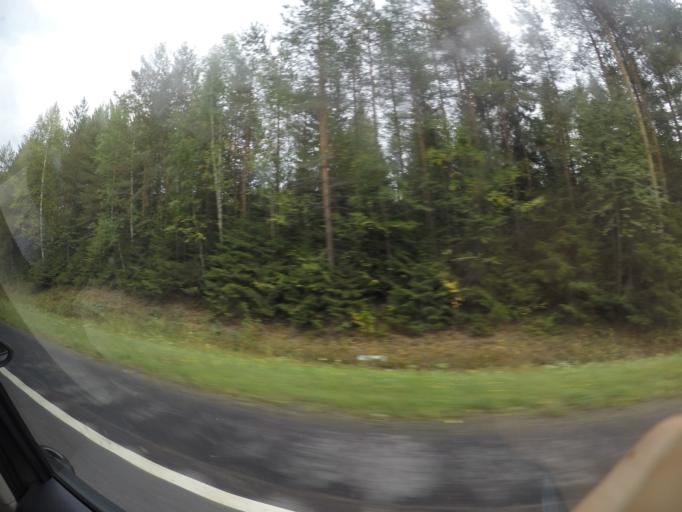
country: FI
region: Haeme
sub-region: Haemeenlinna
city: Parola
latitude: 61.1034
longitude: 24.4087
